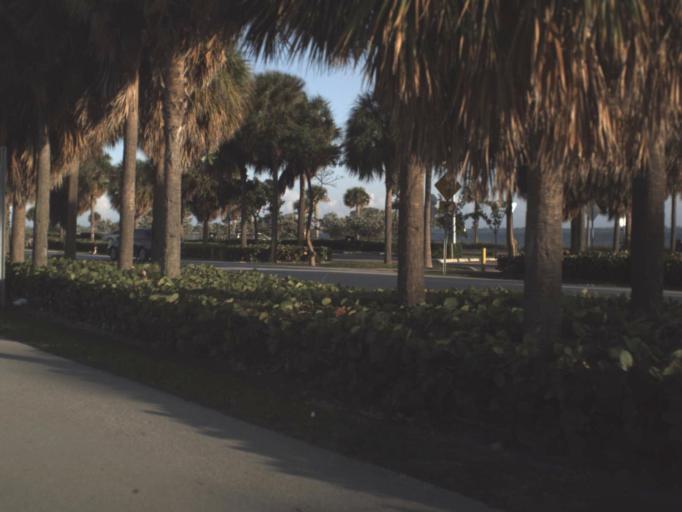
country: US
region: Florida
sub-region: Miami-Dade County
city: Miami
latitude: 25.7463
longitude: -80.1915
